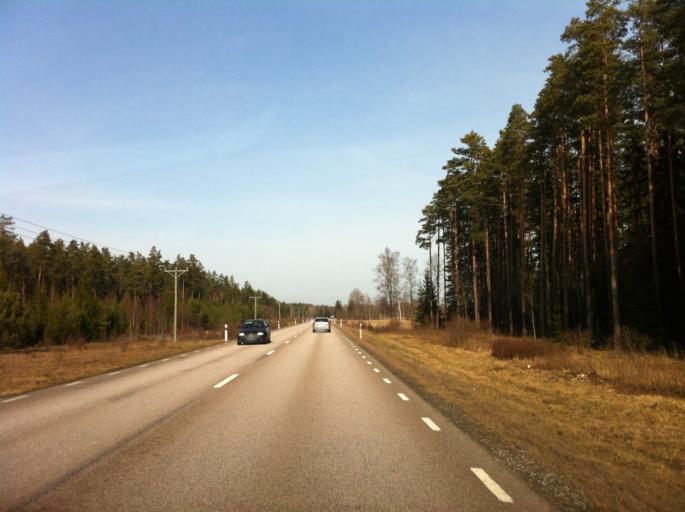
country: SE
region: Joenkoeping
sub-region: Mullsjo Kommun
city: Mullsjoe
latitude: 58.0639
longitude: 13.8595
